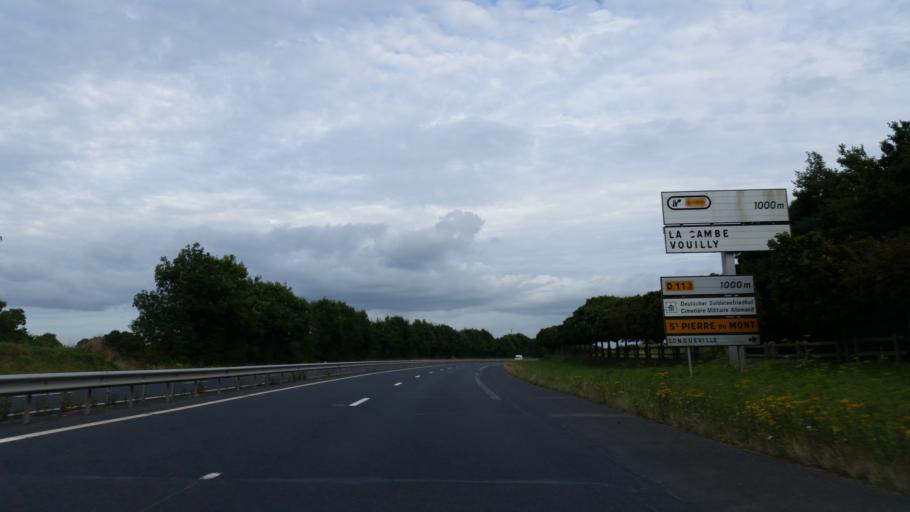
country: FR
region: Lower Normandy
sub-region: Departement du Calvados
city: Grandcamp-Maisy
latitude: 49.3431
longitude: -1.0216
